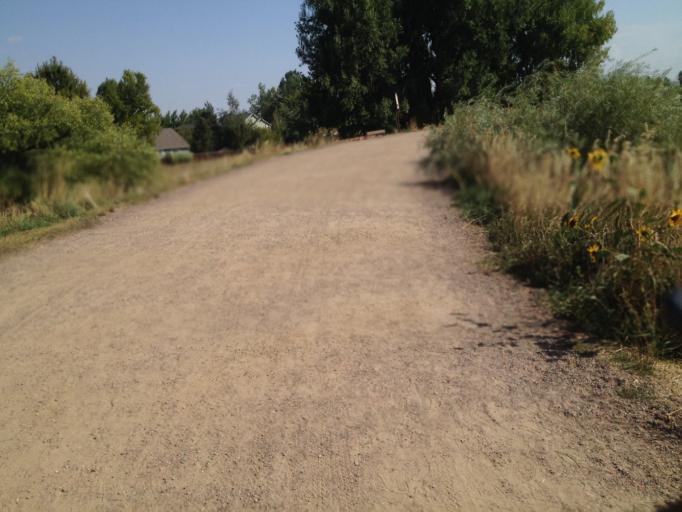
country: US
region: Colorado
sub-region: Boulder County
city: Lafayette
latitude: 39.9966
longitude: -105.1096
